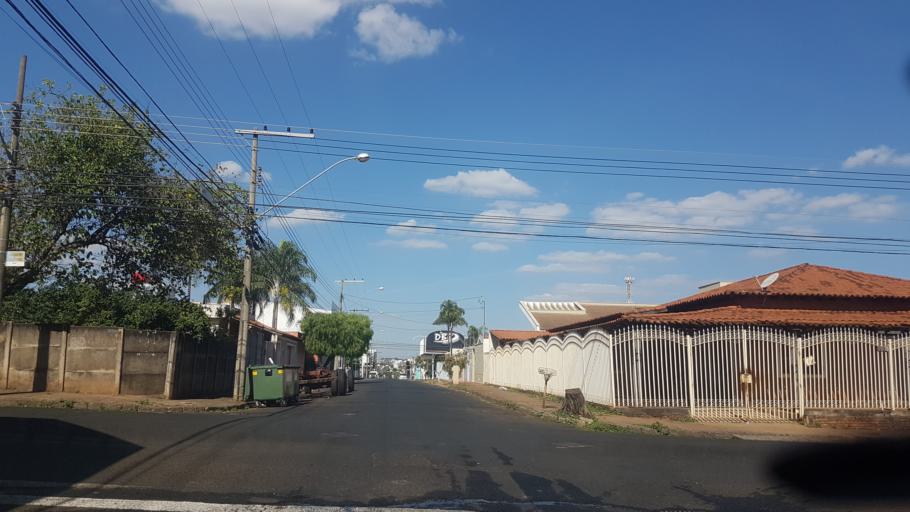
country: BR
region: Minas Gerais
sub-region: Uberlandia
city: Uberlandia
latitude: -18.8953
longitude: -48.2650
